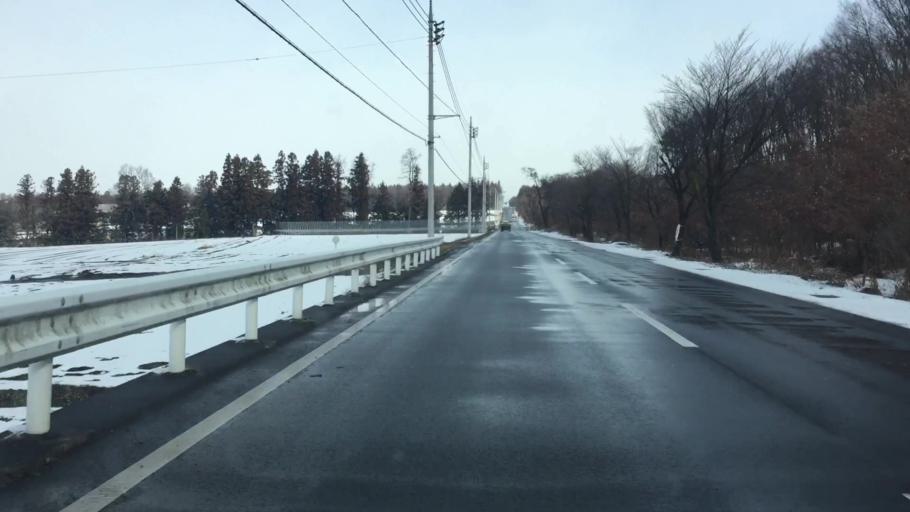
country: JP
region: Gunma
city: Numata
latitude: 36.6159
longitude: 139.0824
